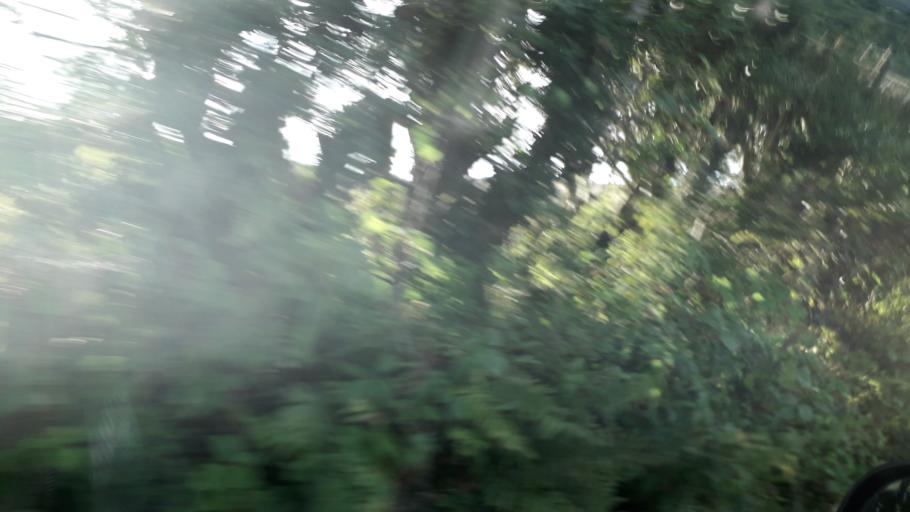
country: GB
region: Northern Ireland
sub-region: Down District
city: Warrenpoint
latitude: 54.0664
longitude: -6.2758
